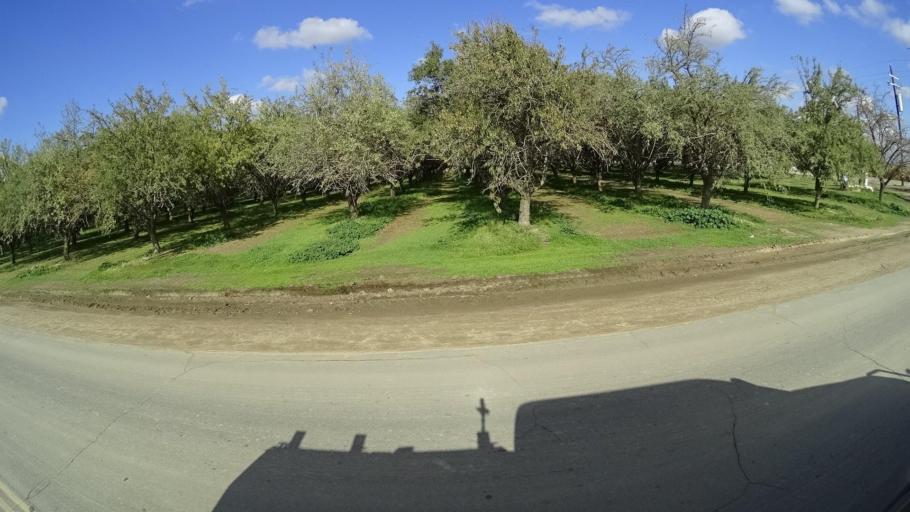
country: US
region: California
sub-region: Kern County
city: McFarland
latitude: 35.6743
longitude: -119.2593
